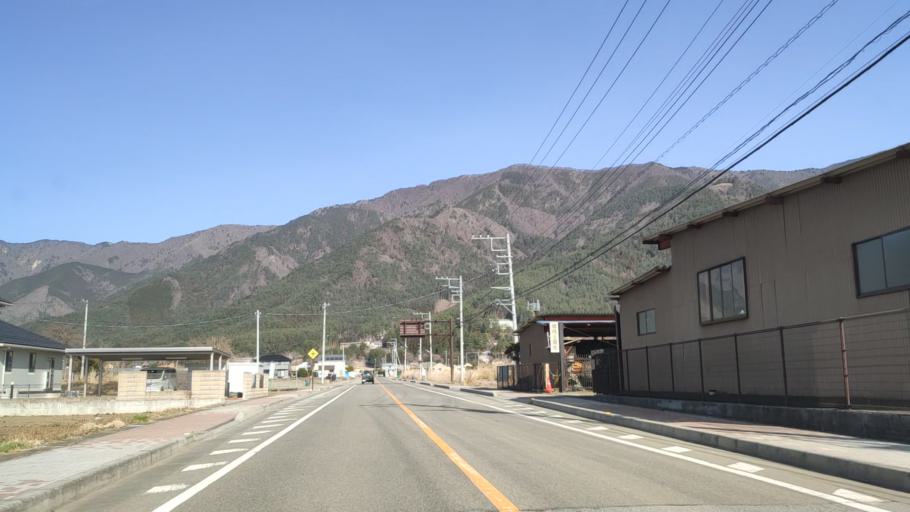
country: JP
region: Yamanashi
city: Fujikawaguchiko
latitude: 35.5212
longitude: 138.7404
